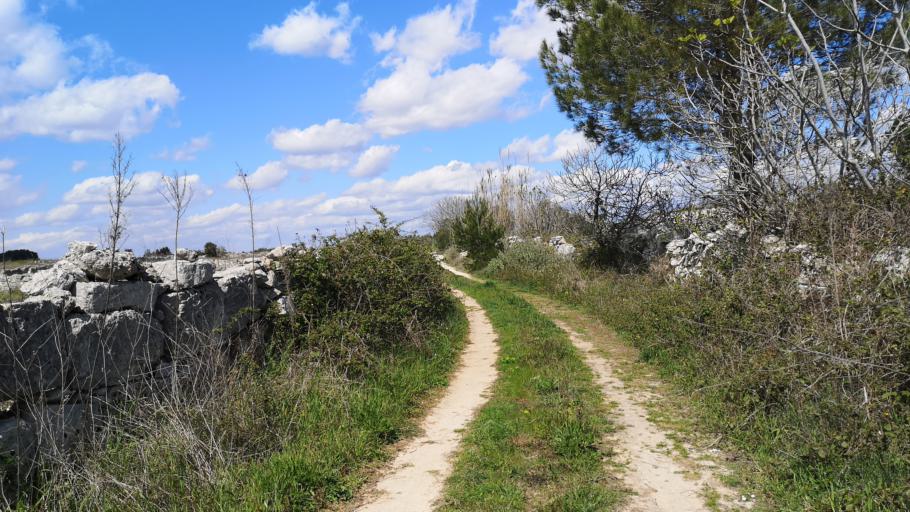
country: IT
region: Apulia
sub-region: Provincia di Lecce
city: Spongano
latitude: 40.0284
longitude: 18.3622
